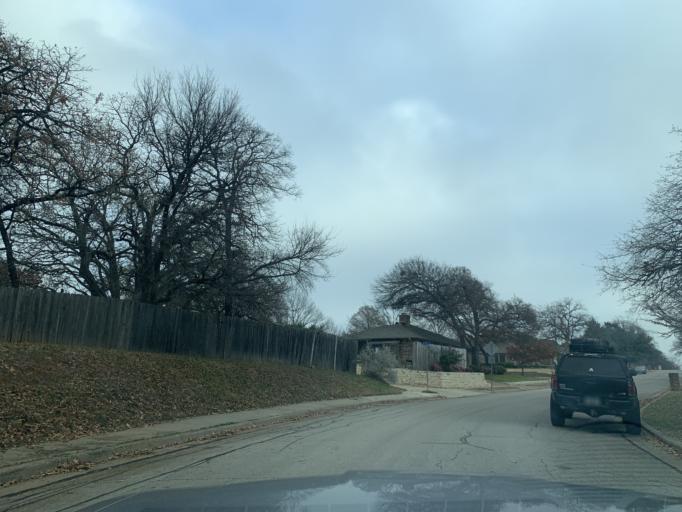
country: US
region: Texas
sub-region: Tarrant County
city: Bedford
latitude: 32.8343
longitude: -97.1505
